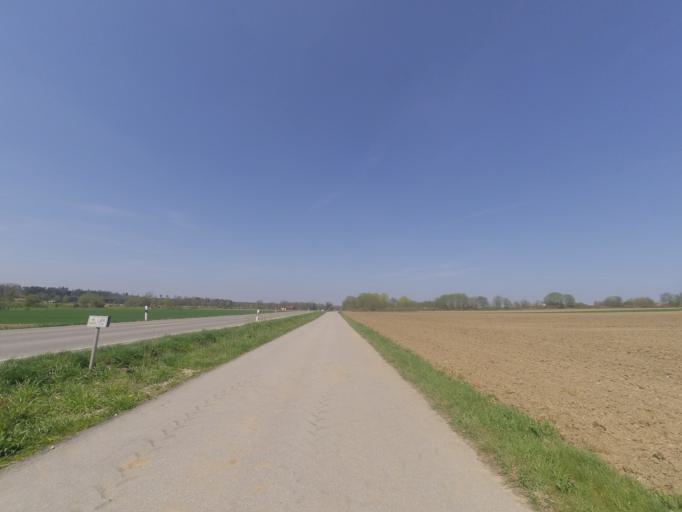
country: DE
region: Bavaria
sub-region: Swabia
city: Weissenhorn
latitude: 48.2809
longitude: 10.1633
